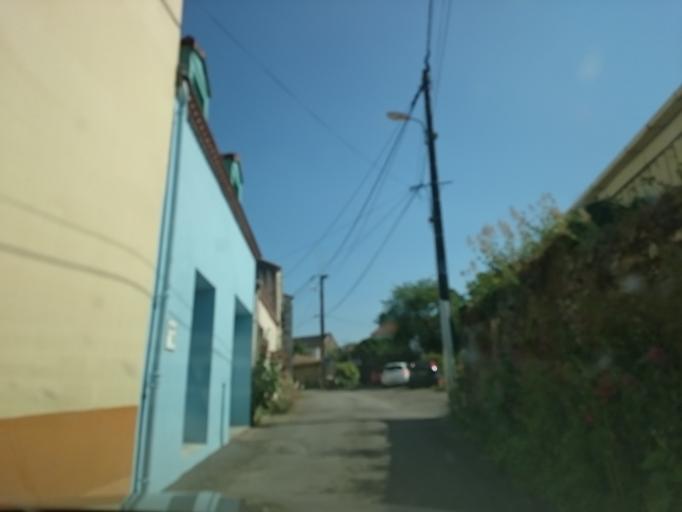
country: FR
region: Pays de la Loire
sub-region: Departement de la Loire-Atlantique
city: Le Pellerin
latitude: 47.2010
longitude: -1.7530
